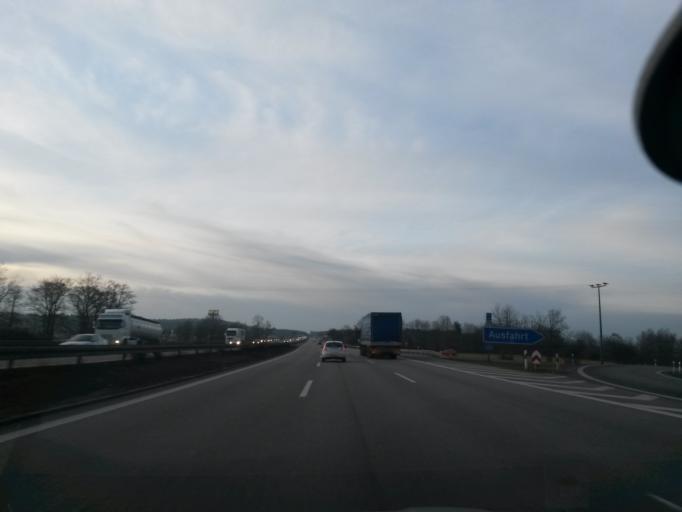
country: DE
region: Bavaria
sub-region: Upper Bavaria
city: Reichertshofen
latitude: 48.6477
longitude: 11.5151
